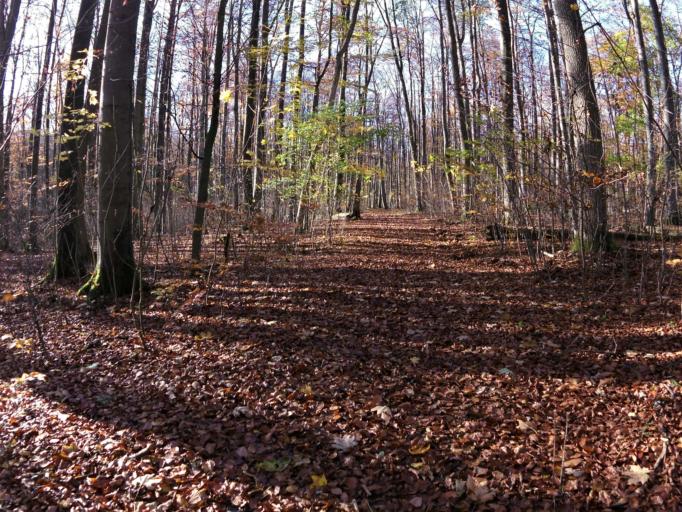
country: DE
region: Thuringia
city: Kammerforst
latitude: 51.0743
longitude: 10.4338
